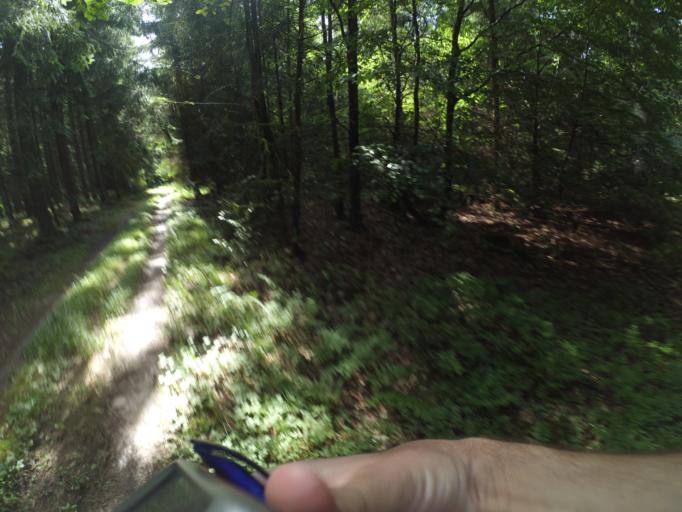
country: DE
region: Hesse
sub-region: Regierungsbezirk Kassel
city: Kirchheim
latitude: 50.8646
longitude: 9.5302
